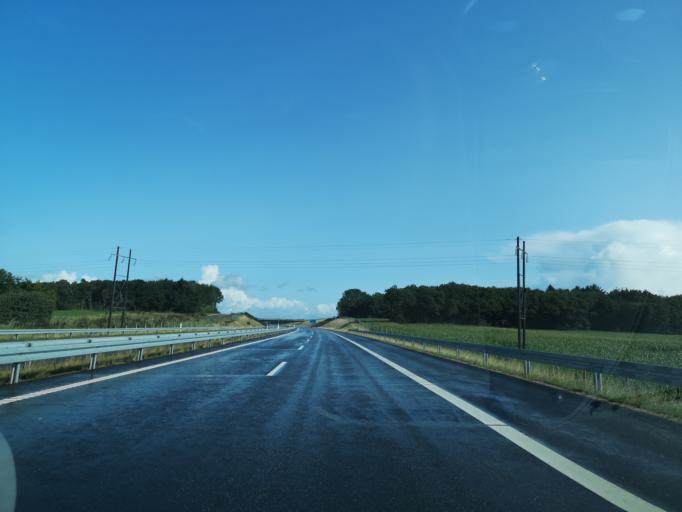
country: DK
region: Central Jutland
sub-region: Herning Kommune
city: Snejbjerg
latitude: 56.1695
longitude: 8.8901
